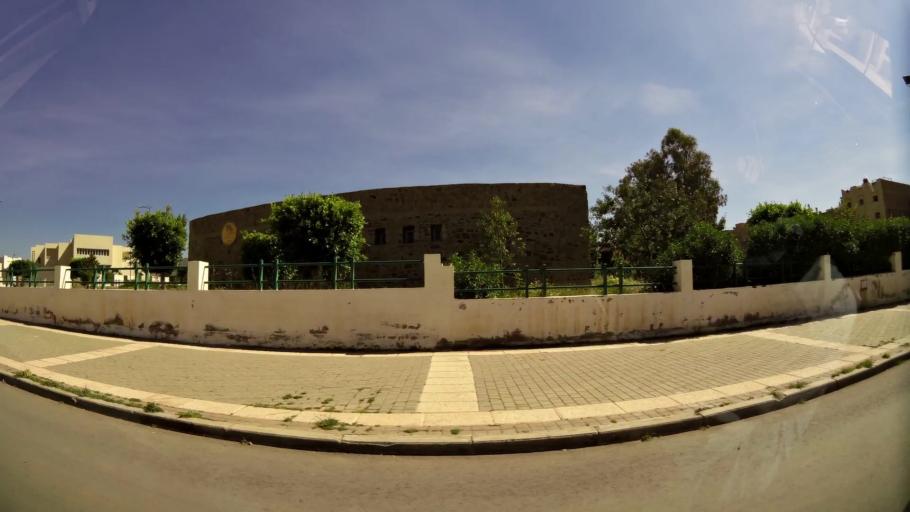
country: MA
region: Oriental
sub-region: Oujda-Angad
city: Oujda
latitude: 34.6602
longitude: -1.9126
